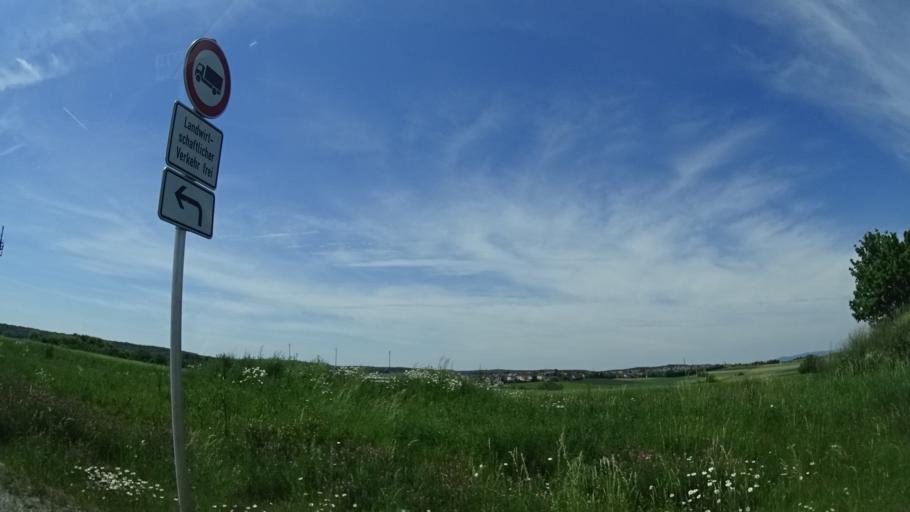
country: DE
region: Bavaria
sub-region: Regierungsbezirk Unterfranken
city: Oerlenbach
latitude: 50.1444
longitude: 10.1498
